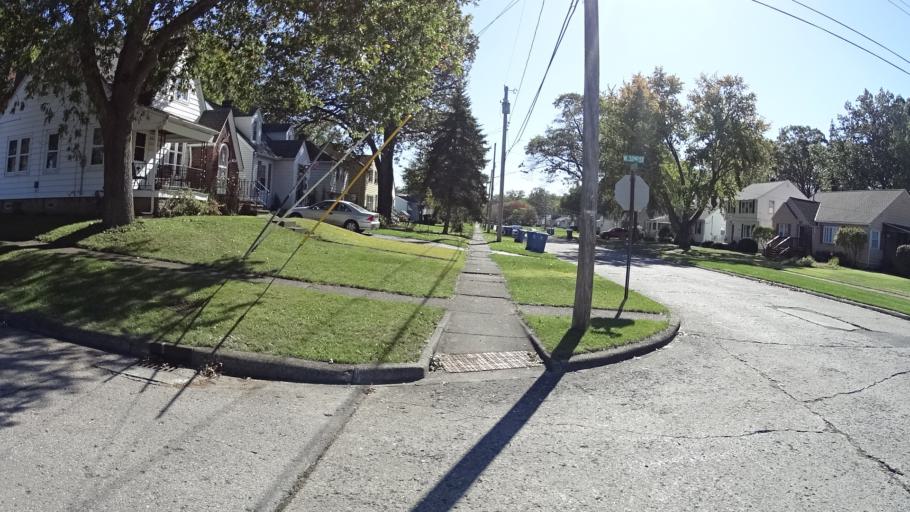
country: US
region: Ohio
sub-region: Lorain County
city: Lorain
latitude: 41.4413
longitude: -82.1729
